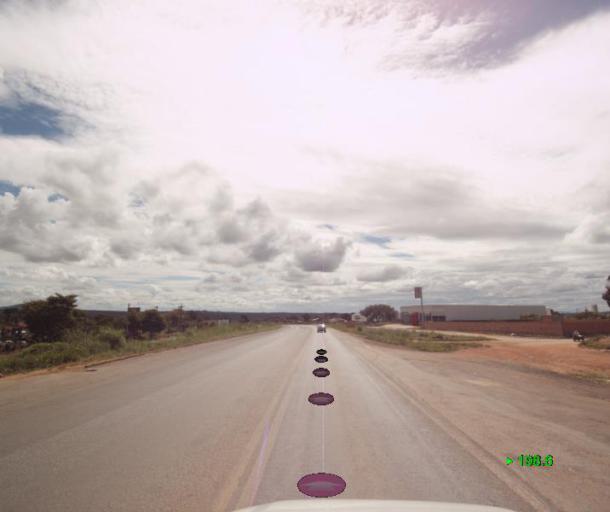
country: BR
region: Goias
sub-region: Uruacu
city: Uruacu
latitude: -14.5153
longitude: -49.1510
